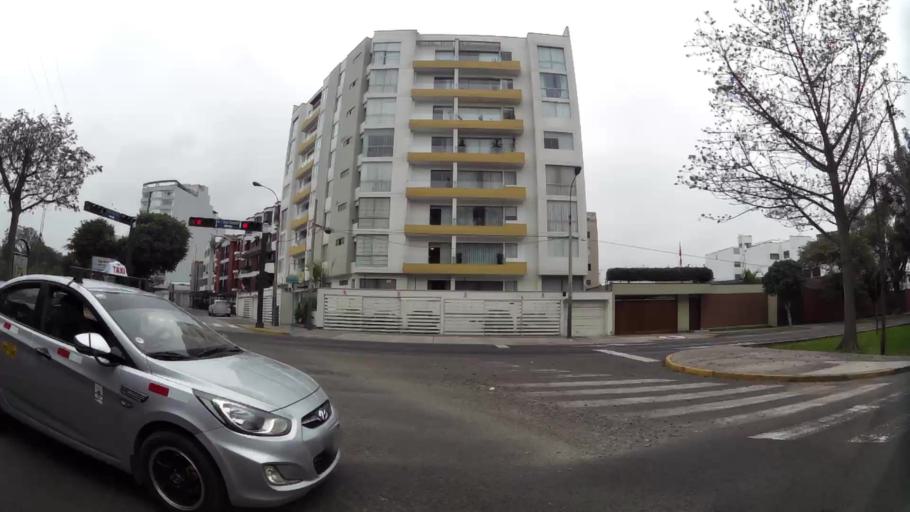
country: PE
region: Lima
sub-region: Lima
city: San Luis
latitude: -12.1040
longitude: -77.0112
